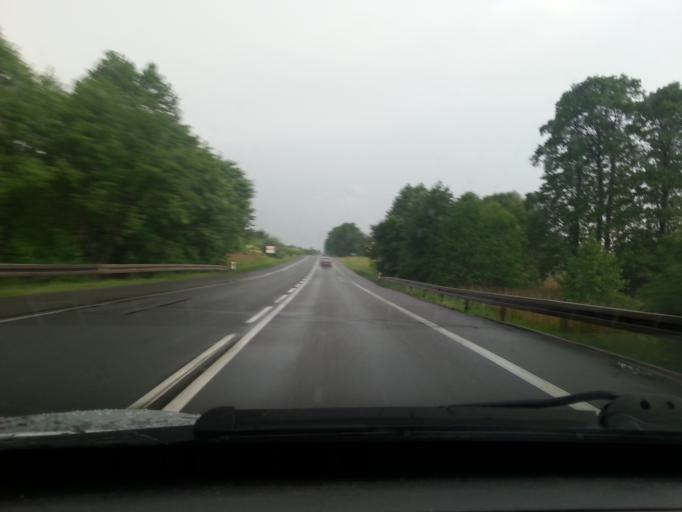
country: PL
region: Lodz Voivodeship
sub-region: Powiat zgierski
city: Strykow
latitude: 51.8635
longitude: 19.5674
